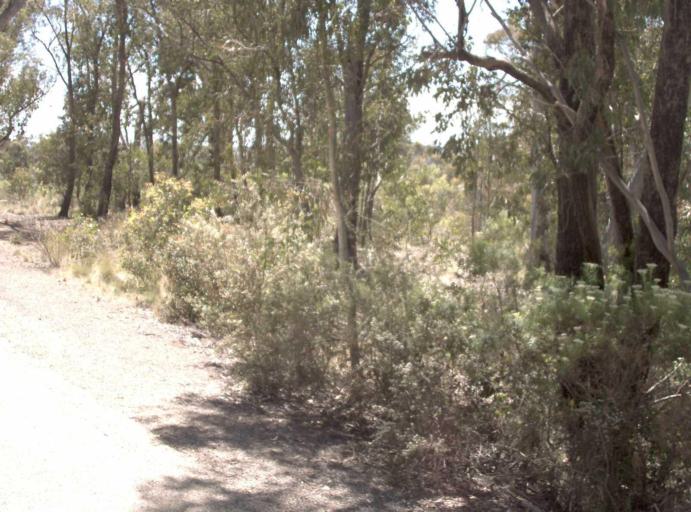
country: AU
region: Victoria
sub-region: East Gippsland
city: Lakes Entrance
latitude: -37.1290
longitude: 148.2449
